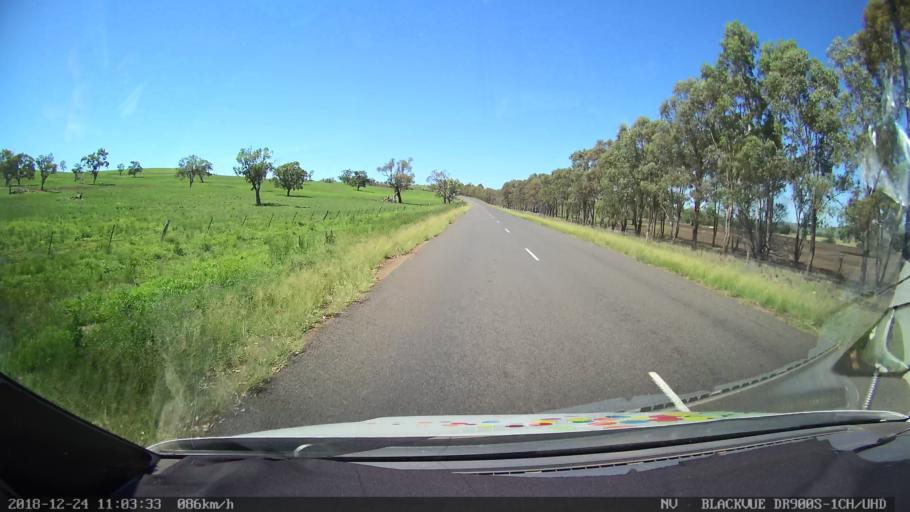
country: AU
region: New South Wales
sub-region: Upper Hunter Shire
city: Merriwa
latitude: -32.0982
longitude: 150.3688
